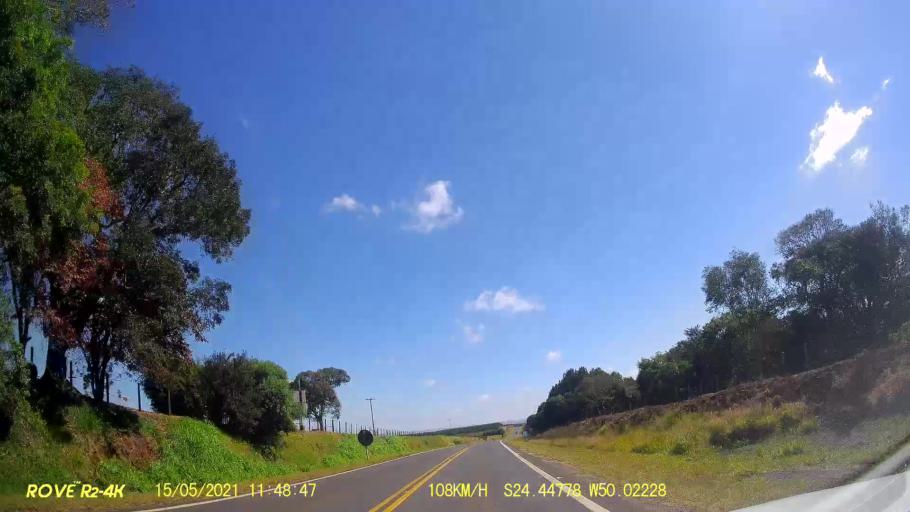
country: BR
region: Parana
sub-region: Pirai Do Sul
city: Pirai do Sul
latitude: -24.4478
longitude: -50.0222
